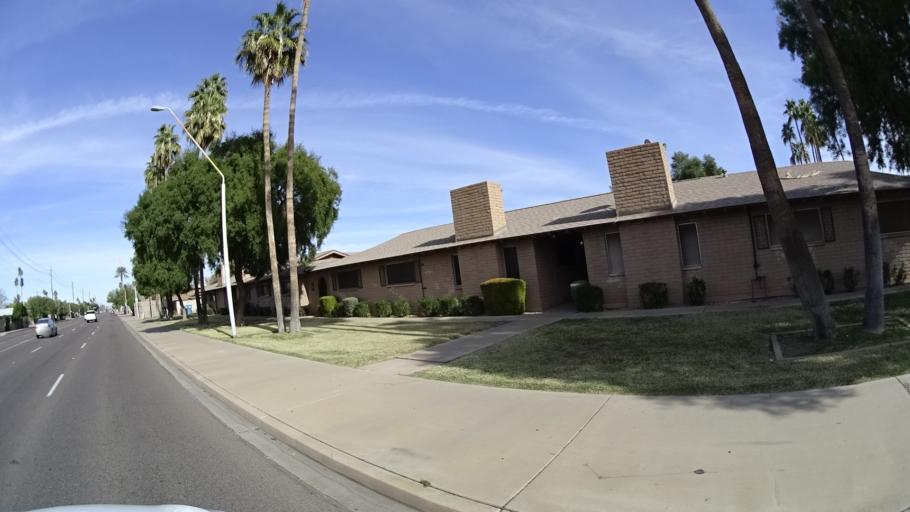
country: US
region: Arizona
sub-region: Maricopa County
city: Tempe Junction
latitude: 33.3958
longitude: -111.9262
